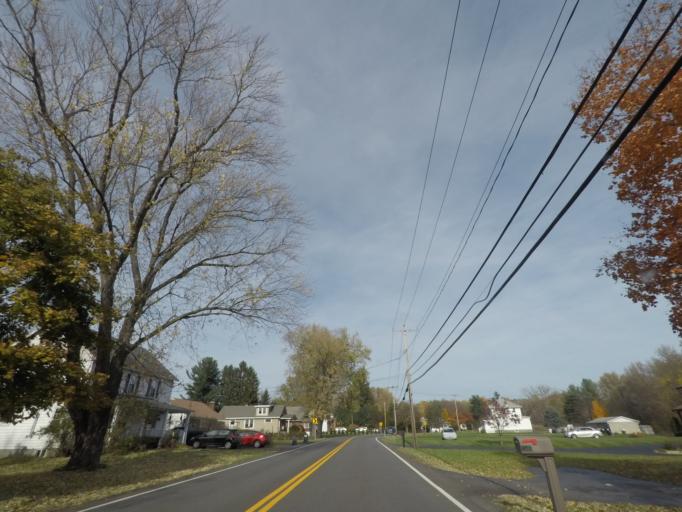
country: US
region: New York
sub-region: Schenectady County
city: Rotterdam
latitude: 42.7643
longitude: -73.9858
